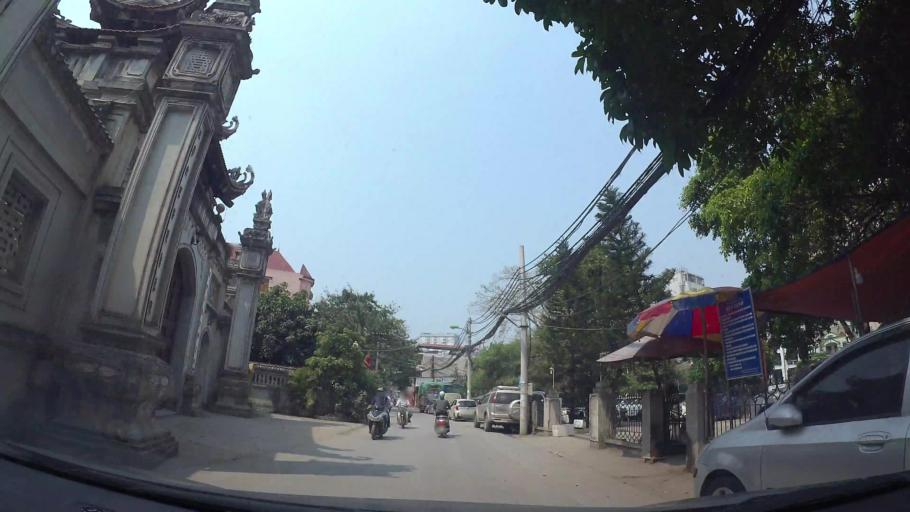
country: VN
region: Ha Noi
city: Thanh Xuan
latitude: 21.0028
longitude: 105.8108
